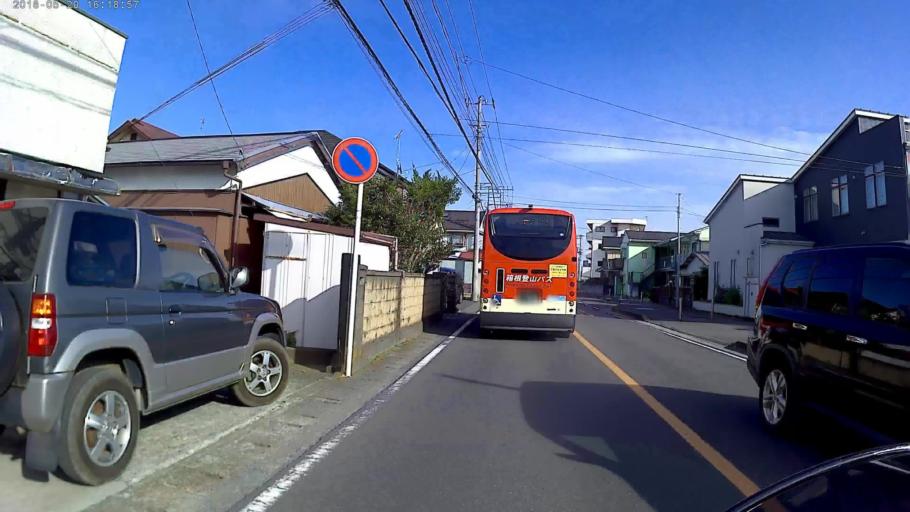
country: JP
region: Kanagawa
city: Odawara
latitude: 35.3004
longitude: 139.1461
